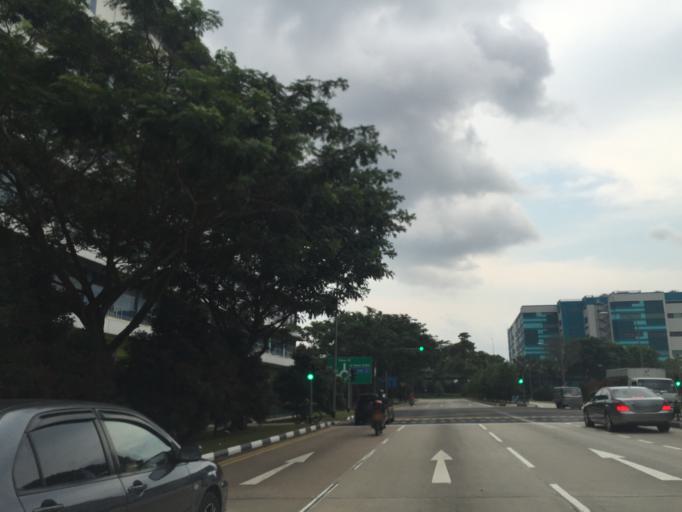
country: MY
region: Johor
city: Johor Bahru
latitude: 1.3250
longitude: 103.6965
